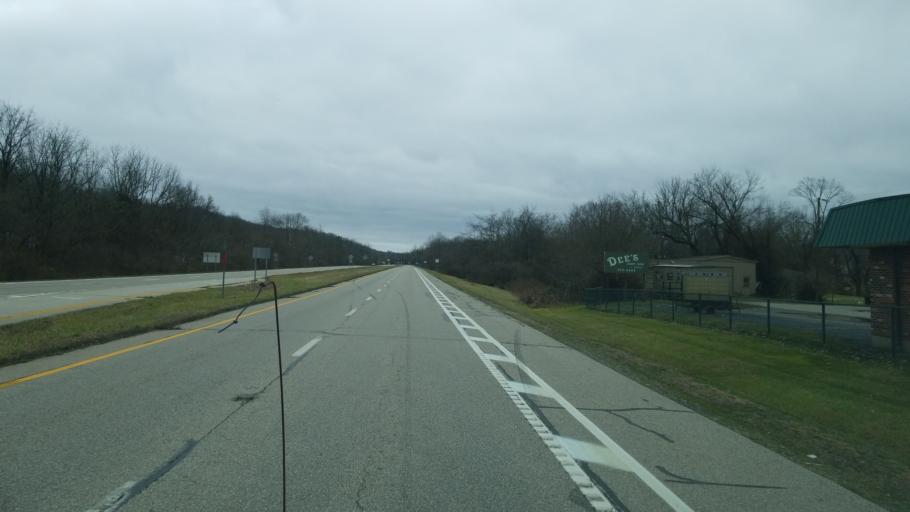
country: US
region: Ohio
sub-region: Clermont County
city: New Richmond
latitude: 38.9476
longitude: -84.2762
